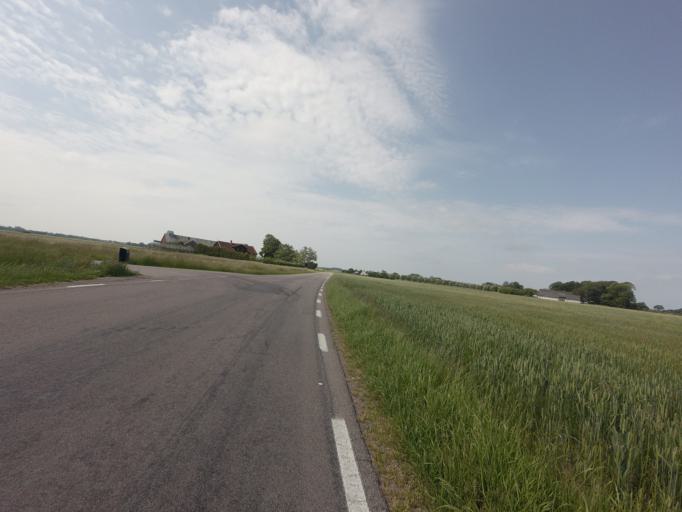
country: SE
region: Skane
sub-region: Helsingborg
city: Odakra
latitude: 56.1959
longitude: 12.6975
